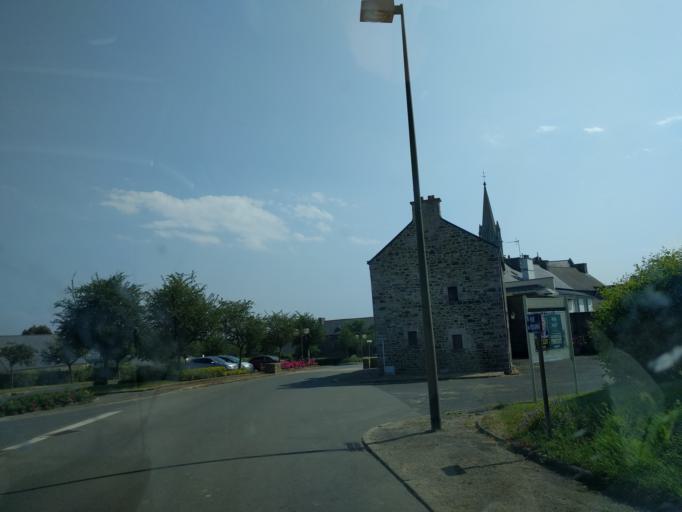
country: FR
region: Brittany
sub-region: Departement des Cotes-d'Armor
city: Lamballe
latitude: 48.5114
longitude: -2.4879
